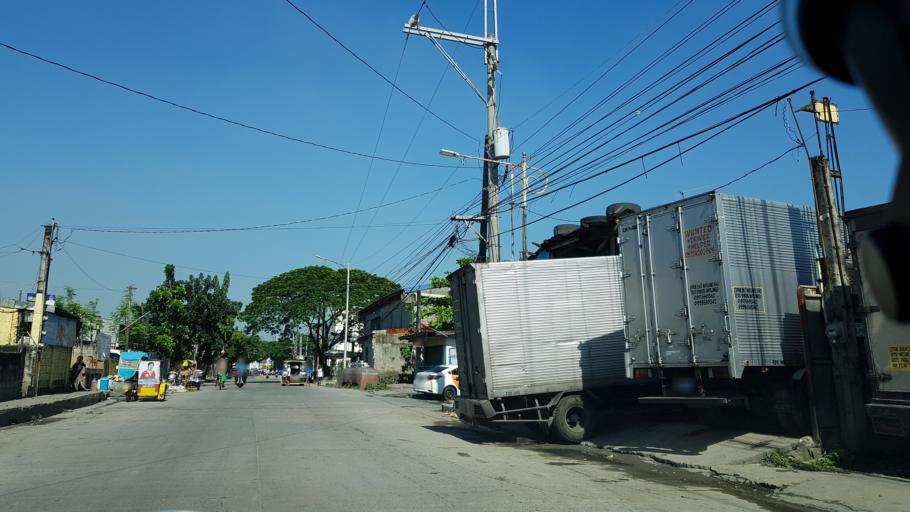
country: PH
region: Metro Manila
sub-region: Pasig
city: Pasig City
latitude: 14.5714
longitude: 121.0899
